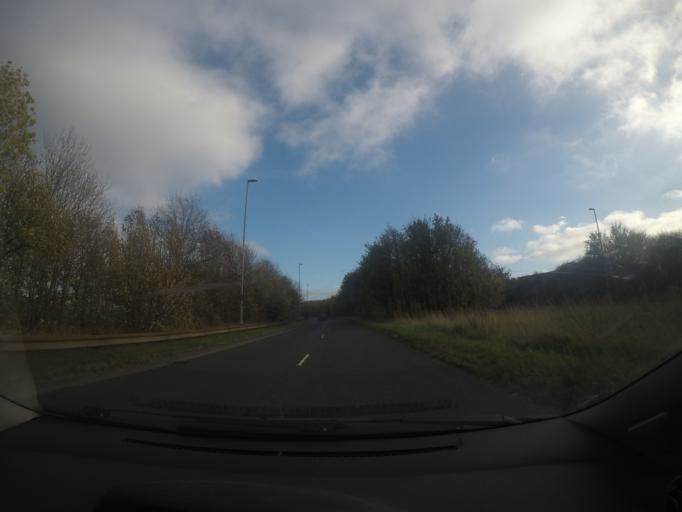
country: GB
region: England
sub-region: City and Borough of Leeds
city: Lofthouse
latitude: 53.7656
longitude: -1.5116
